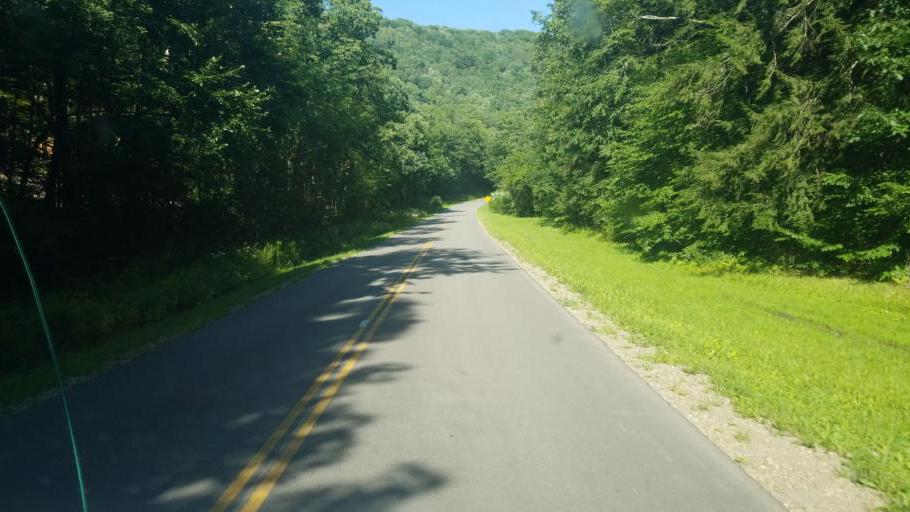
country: US
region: New York
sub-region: Allegany County
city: Wellsville
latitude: 42.0209
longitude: -77.9843
